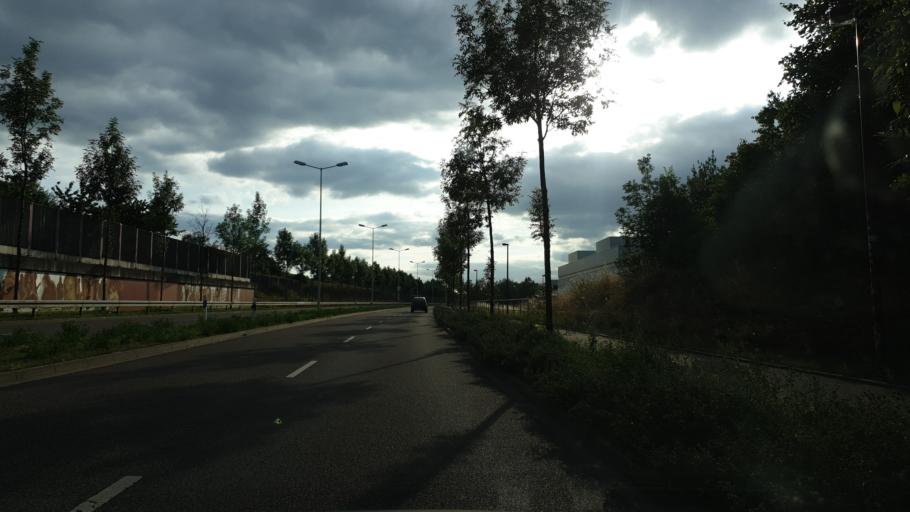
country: DE
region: Saxony
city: Hilbersdorf
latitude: 50.8193
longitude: 12.9743
